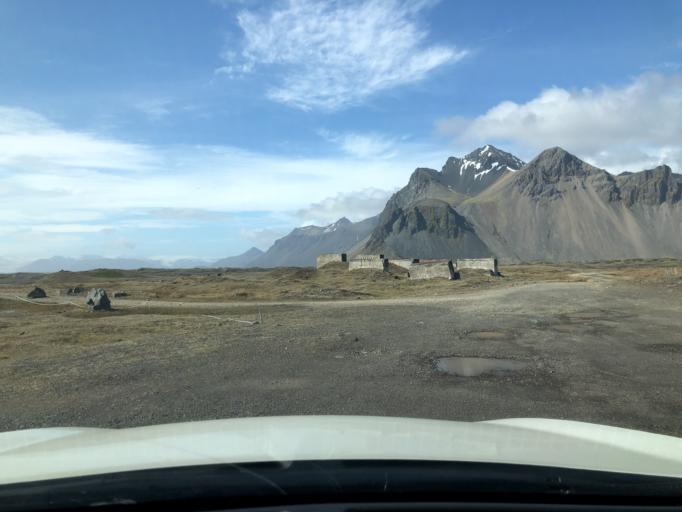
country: IS
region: East
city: Hoefn
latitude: 64.2402
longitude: -14.9713
